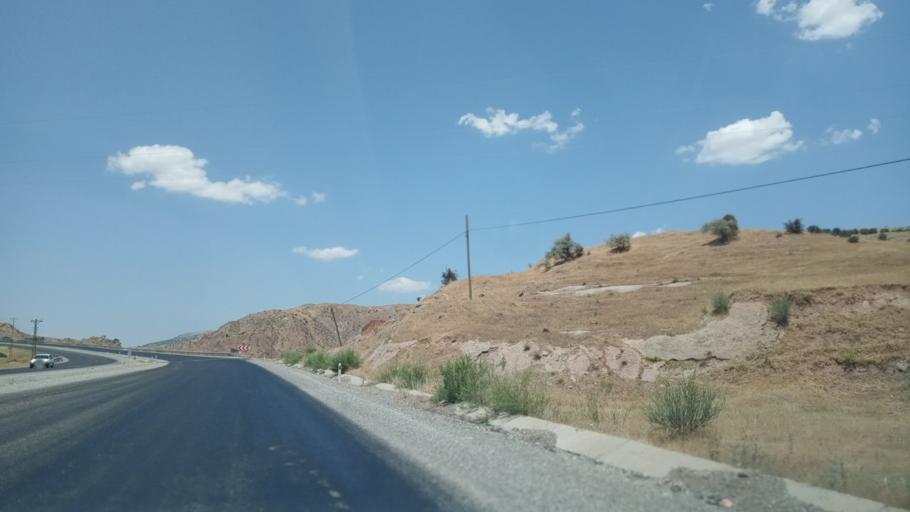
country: TR
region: Batman
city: Kozluk
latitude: 38.1722
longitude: 41.4509
